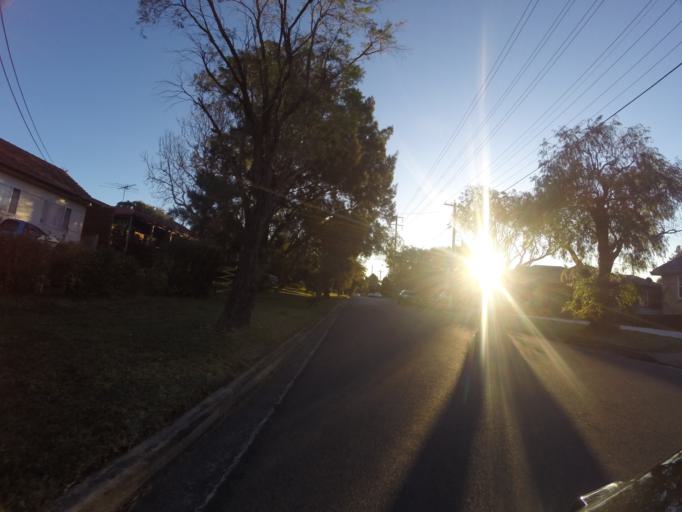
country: AU
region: New South Wales
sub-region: Sutherland Shire
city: Miranda
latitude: -34.0380
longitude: 151.0932
